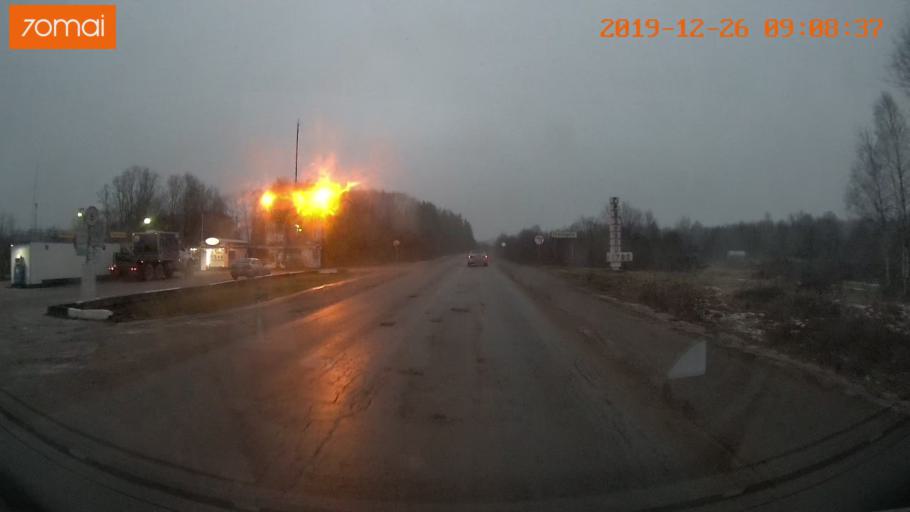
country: RU
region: Vologda
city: Gryazovets
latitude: 58.8586
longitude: 40.2489
